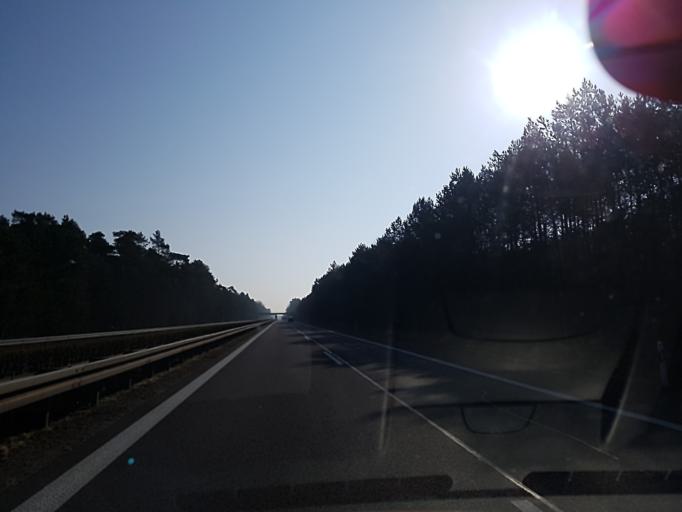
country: DE
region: Brandenburg
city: Forst
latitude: 51.7100
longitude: 14.5648
